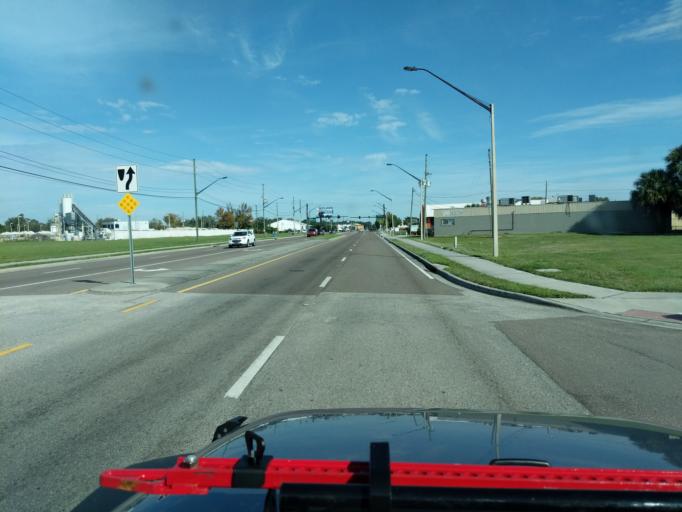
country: US
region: Florida
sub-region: Orange County
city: Winter Garden
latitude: 28.5680
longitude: -81.5734
